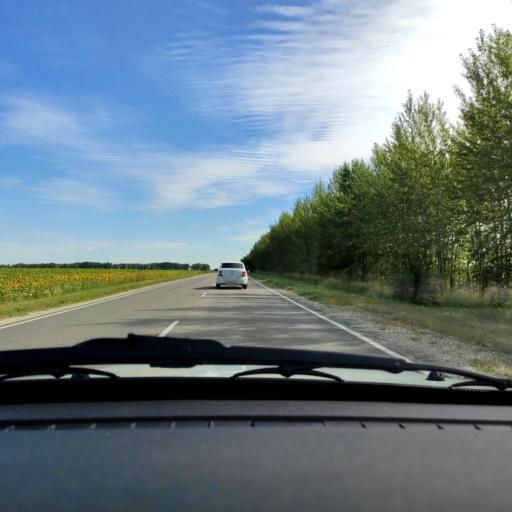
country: RU
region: Voronezj
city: Volya
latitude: 51.7279
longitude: 39.5542
